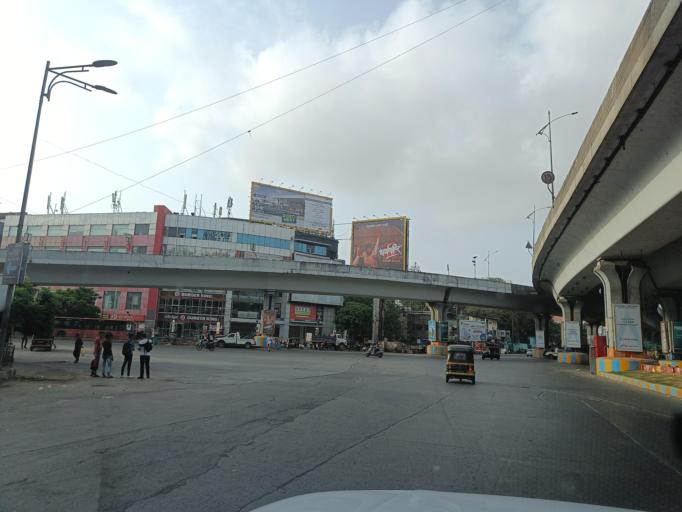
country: IN
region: Maharashtra
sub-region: Thane
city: Thane
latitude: 19.2179
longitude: 72.9783
